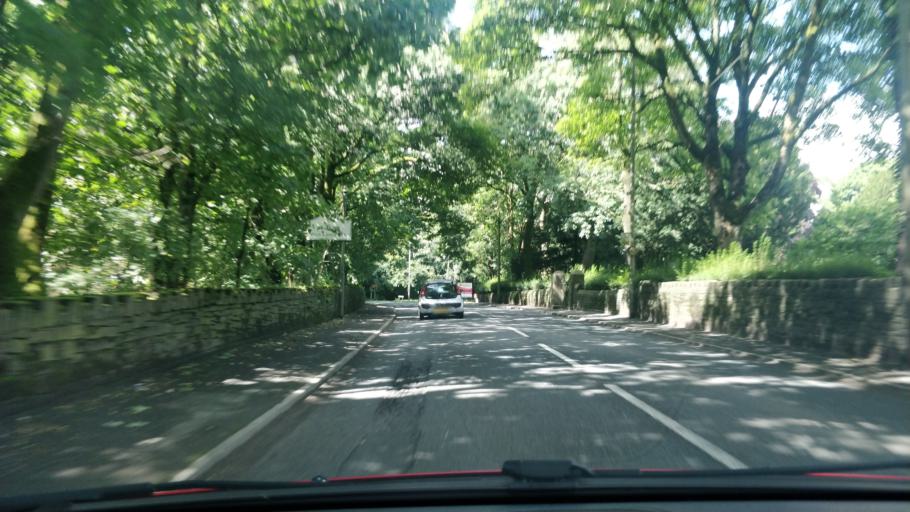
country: GB
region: England
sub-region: Borough of Wigan
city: Shevington
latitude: 53.5921
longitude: -2.7005
